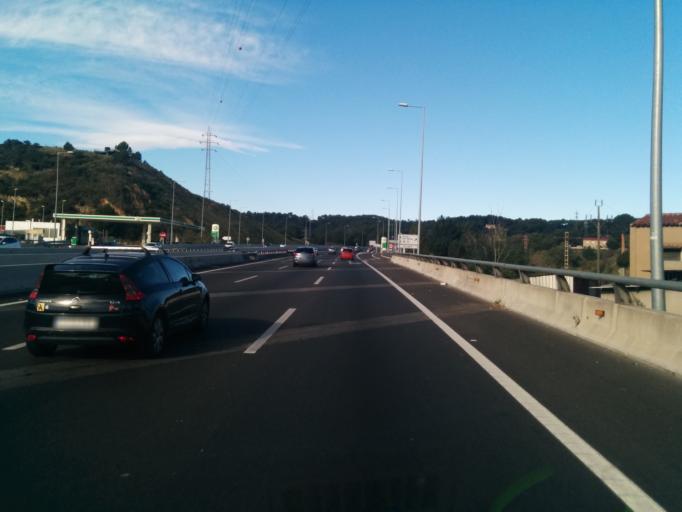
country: ES
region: Catalonia
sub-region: Provincia de Barcelona
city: Montcada i Reixac
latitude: 41.4693
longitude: 2.1689
